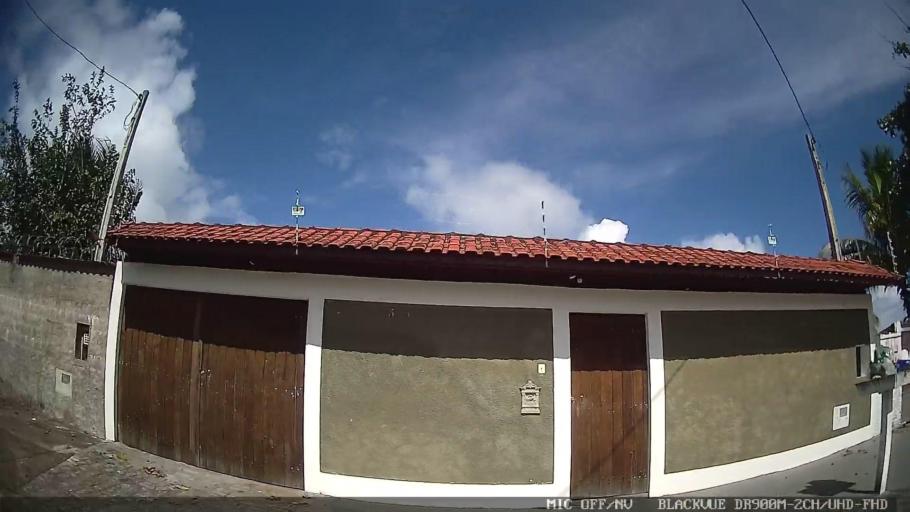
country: BR
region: Sao Paulo
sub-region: Itanhaem
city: Itanhaem
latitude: -24.2355
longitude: -46.8885
